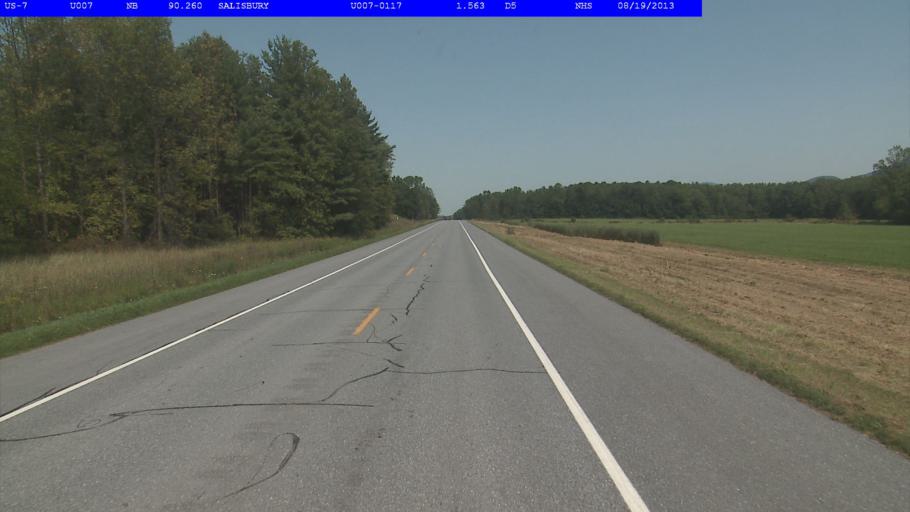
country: US
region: Vermont
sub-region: Addison County
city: Middlebury (village)
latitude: 43.9144
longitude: -73.1115
